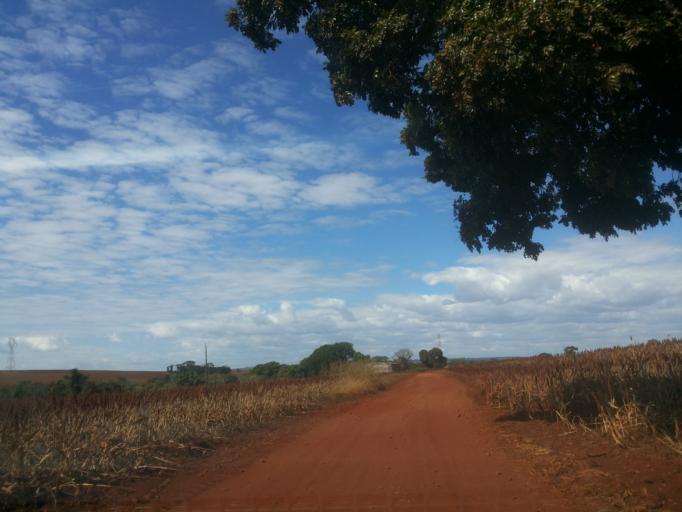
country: BR
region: Minas Gerais
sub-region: Centralina
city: Centralina
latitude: -18.5554
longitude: -49.2362
